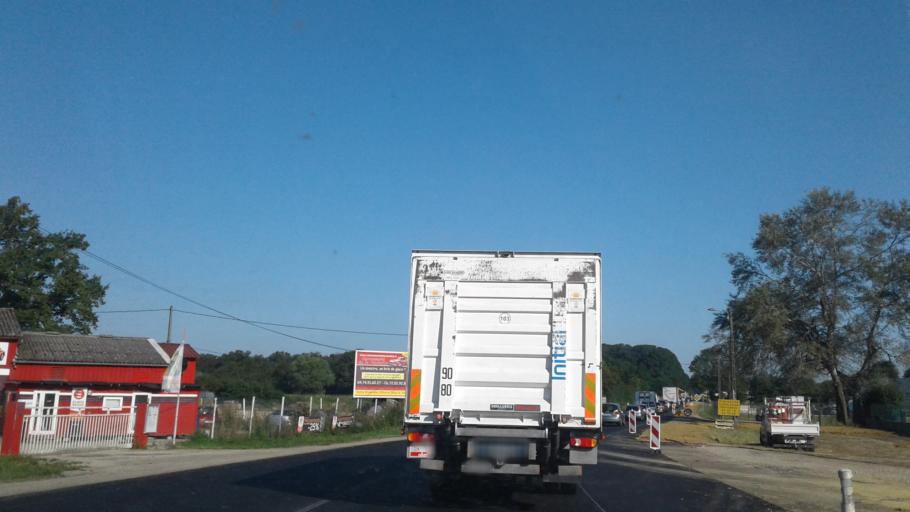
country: FR
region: Rhone-Alpes
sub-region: Departement de l'Ain
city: Montagnat
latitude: 46.1565
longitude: 5.2737
